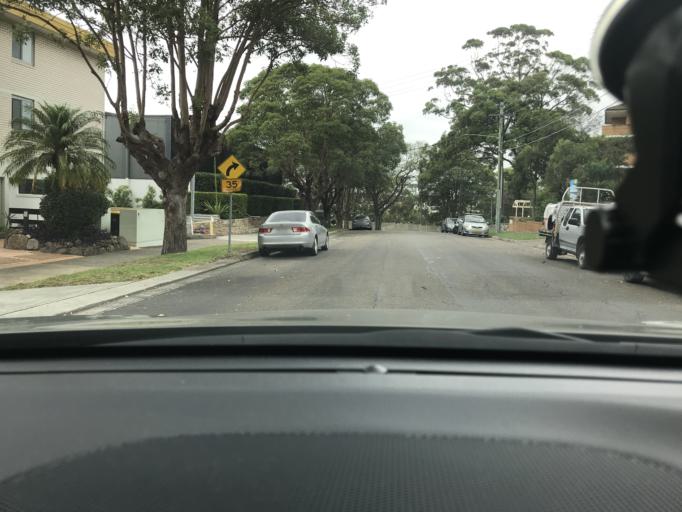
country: AU
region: New South Wales
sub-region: Canada Bay
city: Wareemba
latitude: -33.8474
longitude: 151.1314
